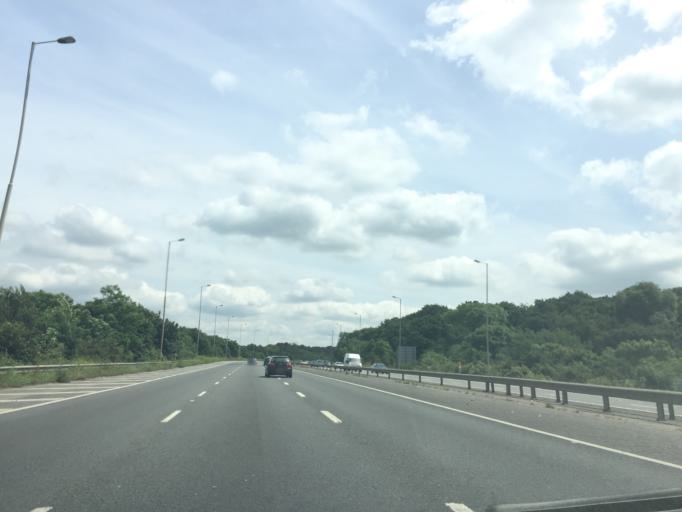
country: GB
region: England
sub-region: Greater London
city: Bexley
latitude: 51.4441
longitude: 0.1635
